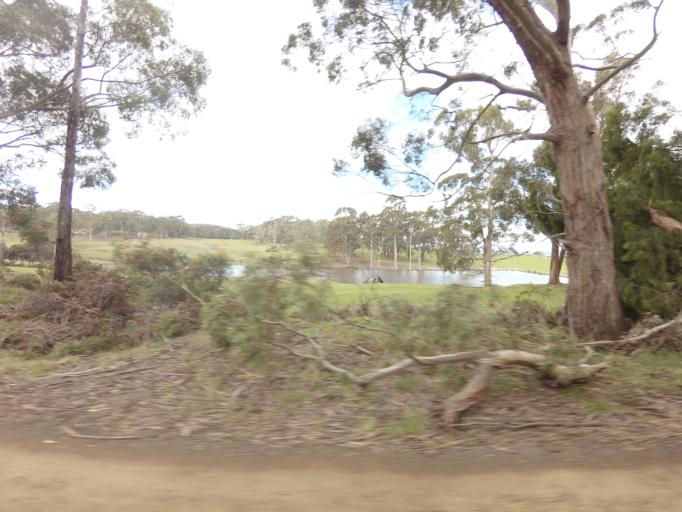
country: AU
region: Tasmania
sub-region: Huon Valley
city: Geeveston
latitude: -43.4263
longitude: 146.9971
